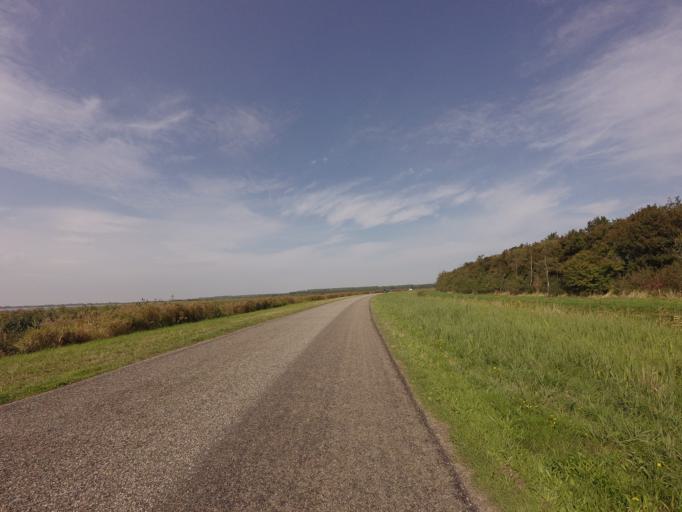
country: NL
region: Groningen
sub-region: Gemeente De Marne
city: Ulrum
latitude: 53.3579
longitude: 6.2618
